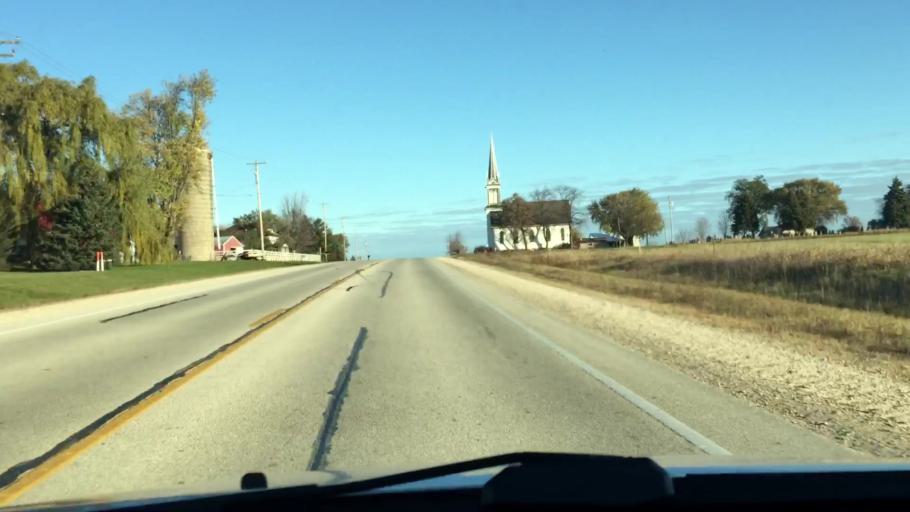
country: US
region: Wisconsin
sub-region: Dodge County
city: Theresa
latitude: 43.5492
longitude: -88.4432
